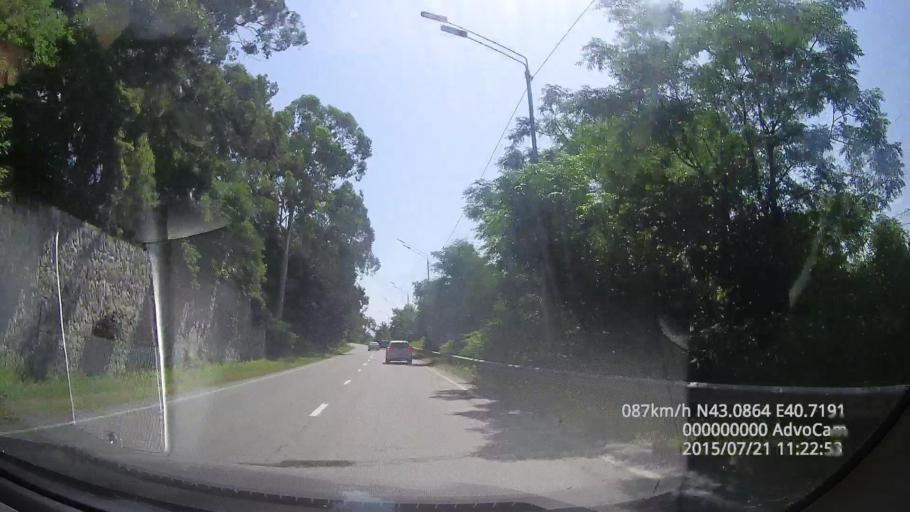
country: GE
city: P'rimorsk'oe
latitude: 43.0863
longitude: 40.7194
